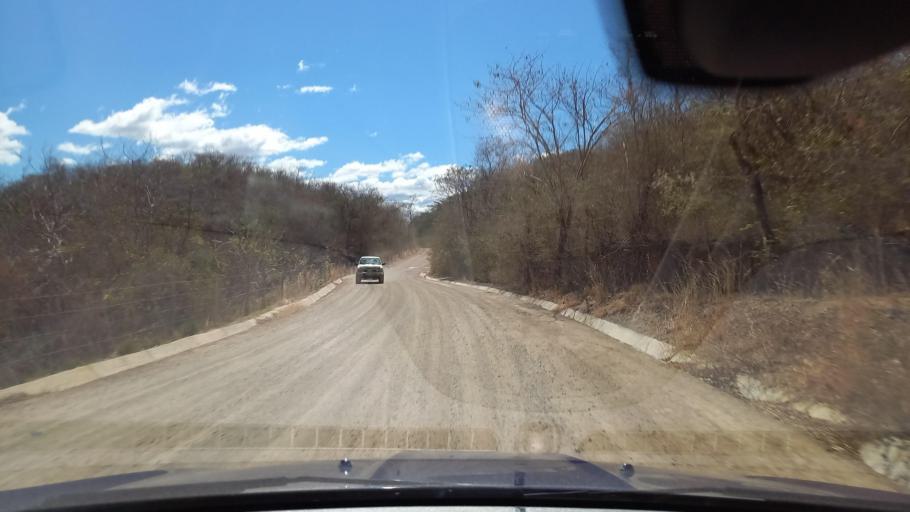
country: SV
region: Santa Ana
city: Metapan
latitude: 14.3588
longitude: -89.4805
